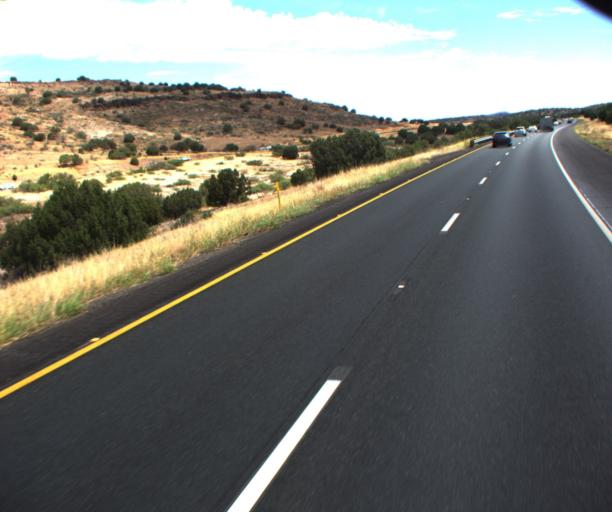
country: US
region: Arizona
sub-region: Yavapai County
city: Camp Verde
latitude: 34.4829
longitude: -112.0161
